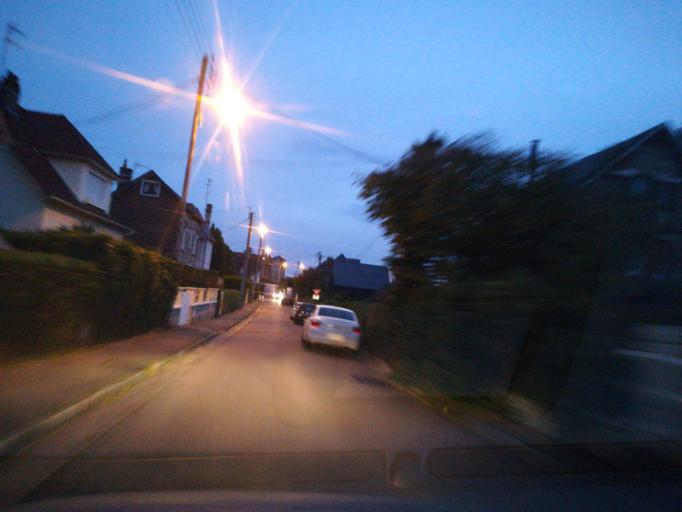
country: FR
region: Haute-Normandie
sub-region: Departement de la Seine-Maritime
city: Mont-Saint-Aignan
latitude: 49.4605
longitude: 1.0908
